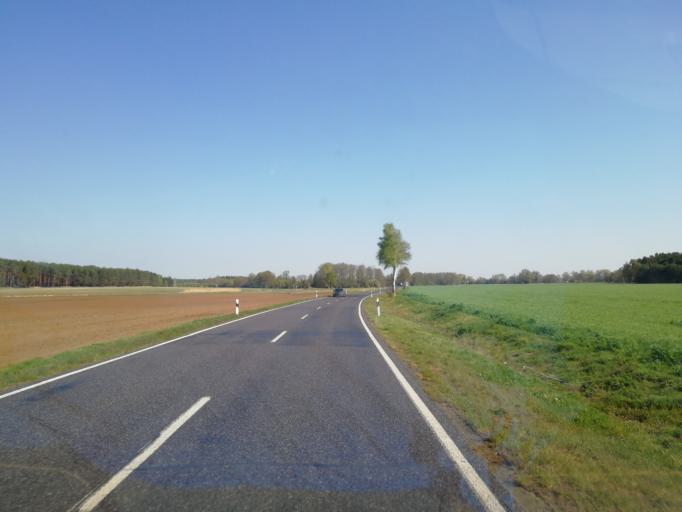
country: DE
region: Brandenburg
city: Crinitz
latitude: 51.7475
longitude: 13.8558
